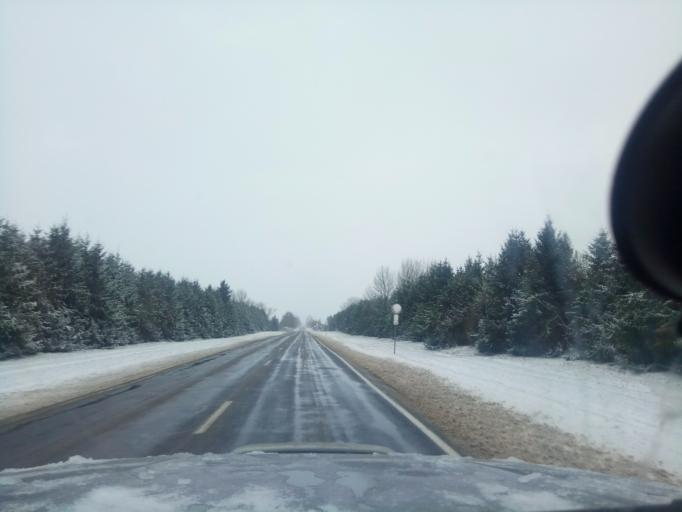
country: BY
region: Minsk
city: Haradzyeya
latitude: 53.3632
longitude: 26.5133
